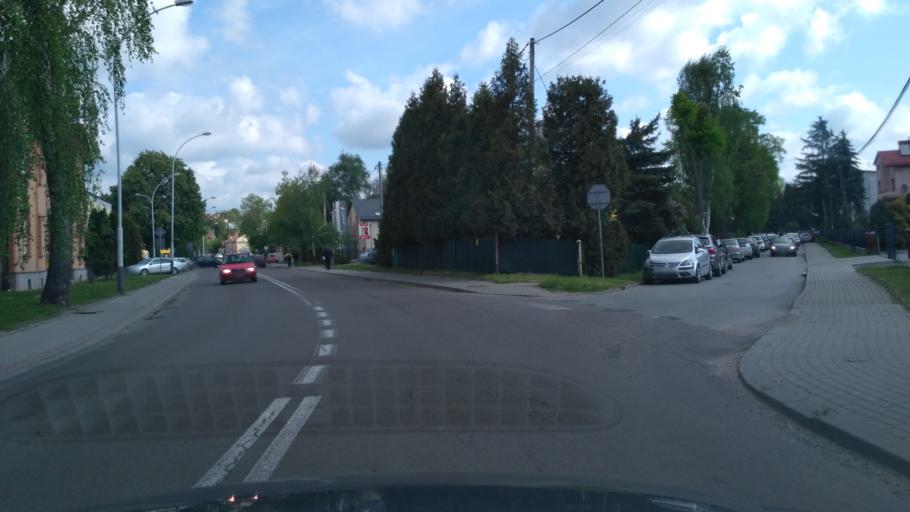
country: PL
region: Subcarpathian Voivodeship
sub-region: Powiat przeworski
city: Przeworsk
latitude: 50.0523
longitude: 22.4919
